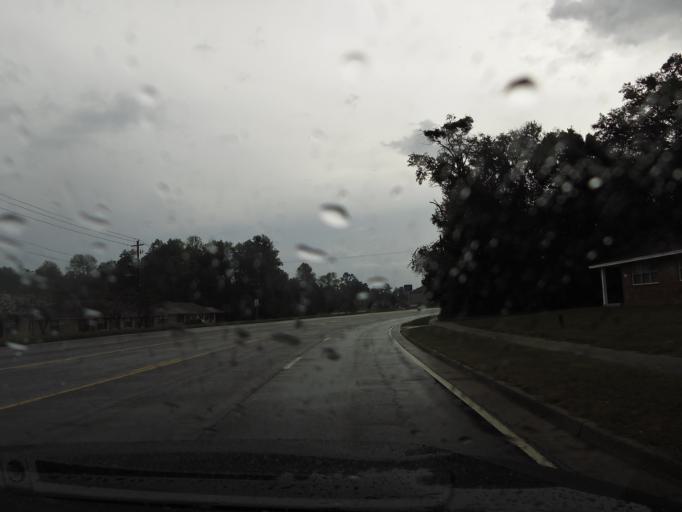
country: US
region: Georgia
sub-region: Wayne County
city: Jesup
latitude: 31.5994
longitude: -81.8711
